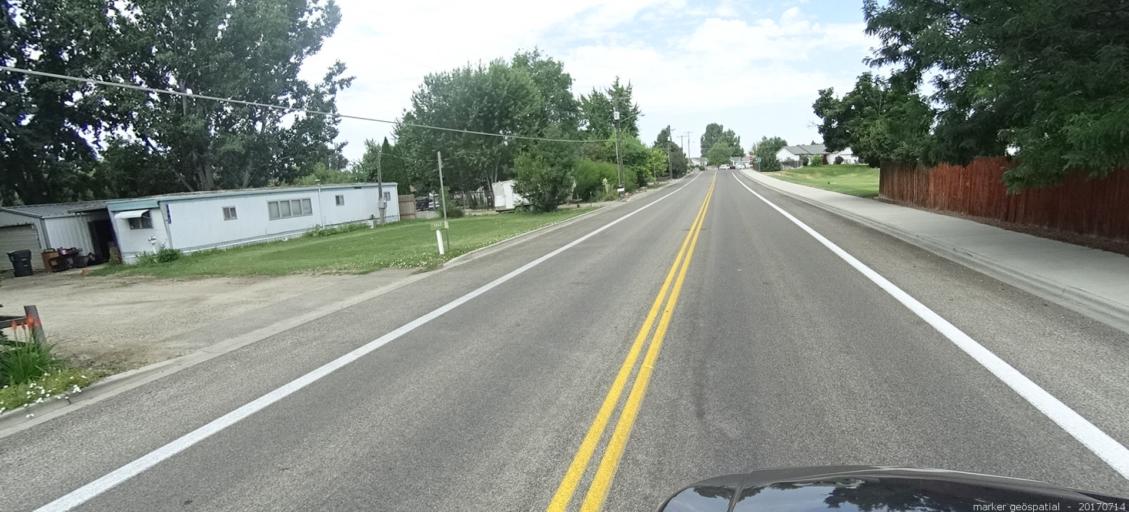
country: US
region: Idaho
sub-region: Ada County
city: Kuna
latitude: 43.4920
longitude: -116.4316
